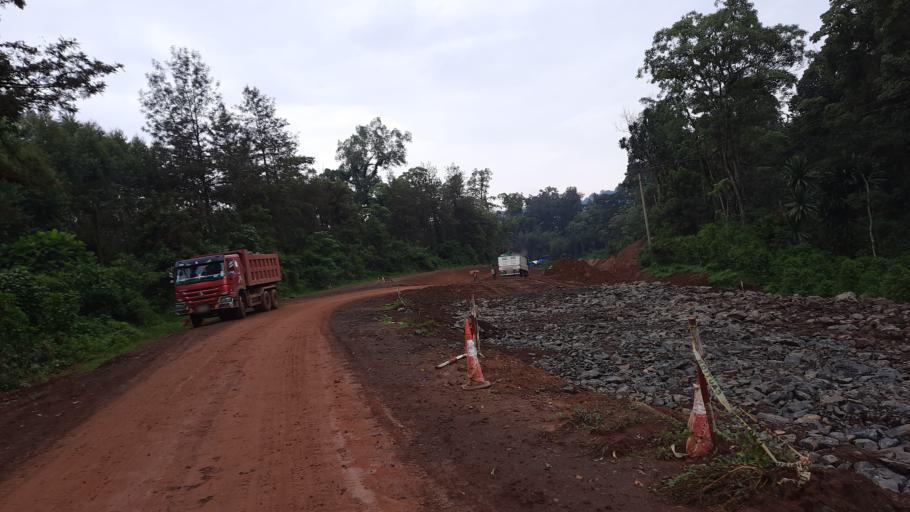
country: ET
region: Oromiya
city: Gore
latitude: 7.8631
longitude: 35.4781
